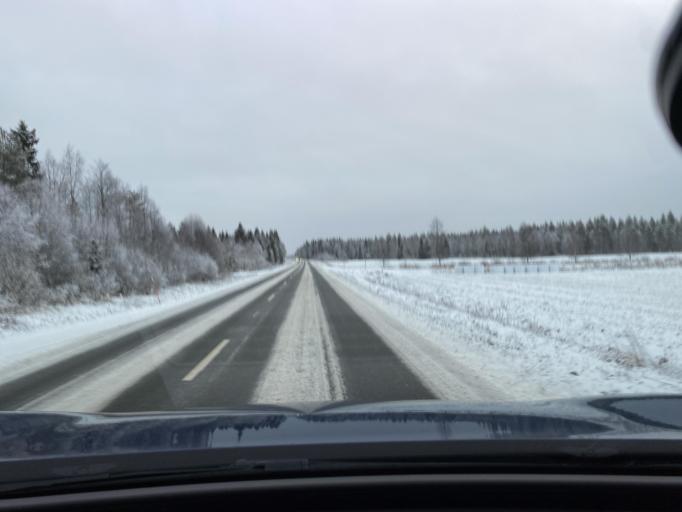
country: FI
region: Lapland
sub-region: Rovaniemi
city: Ranua
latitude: 65.9853
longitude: 26.1622
